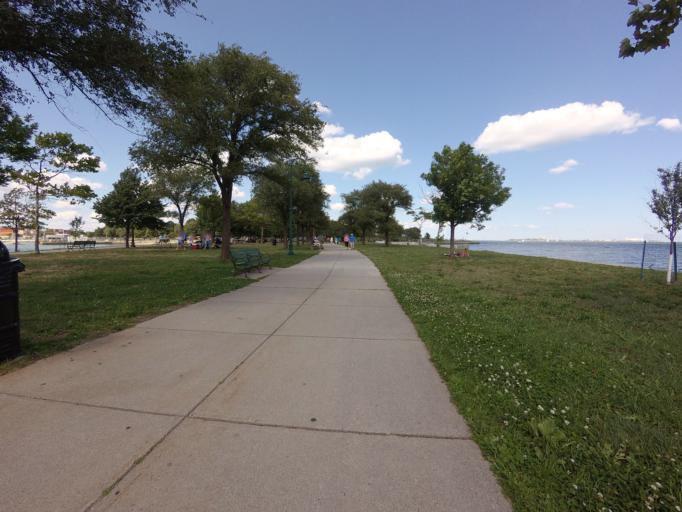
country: US
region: Massachusetts
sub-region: Suffolk County
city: South Boston
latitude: 42.3352
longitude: -71.0122
